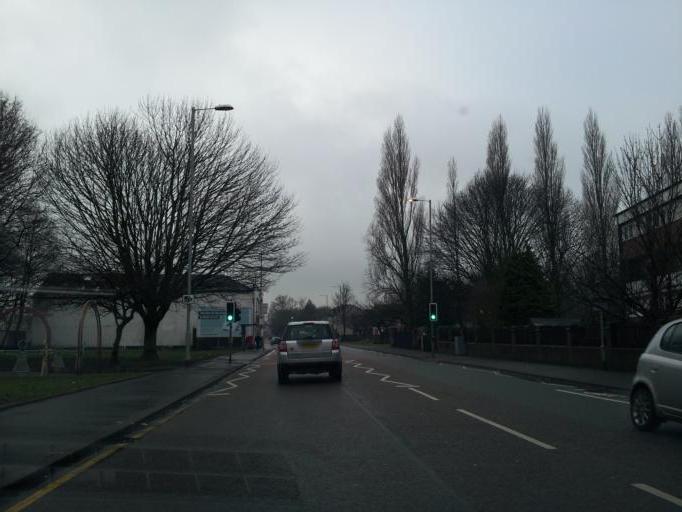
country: GB
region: England
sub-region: Manchester
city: Blackley
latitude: 53.5072
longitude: -2.2176
